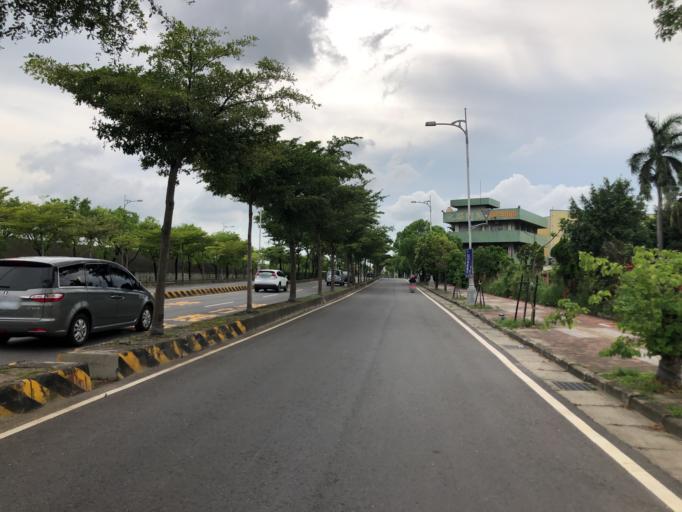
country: TW
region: Taiwan
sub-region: Taichung City
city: Taichung
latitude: 24.0935
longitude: 120.6427
